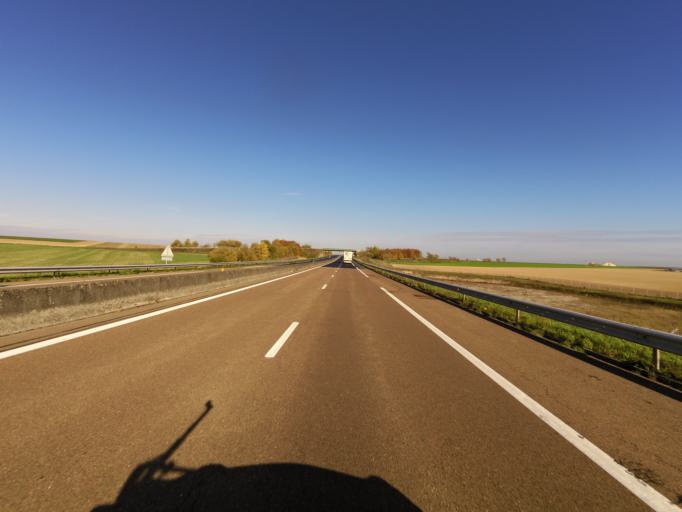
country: FR
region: Champagne-Ardenne
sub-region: Departement de la Marne
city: Fagnieres
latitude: 48.9192
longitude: 4.2833
